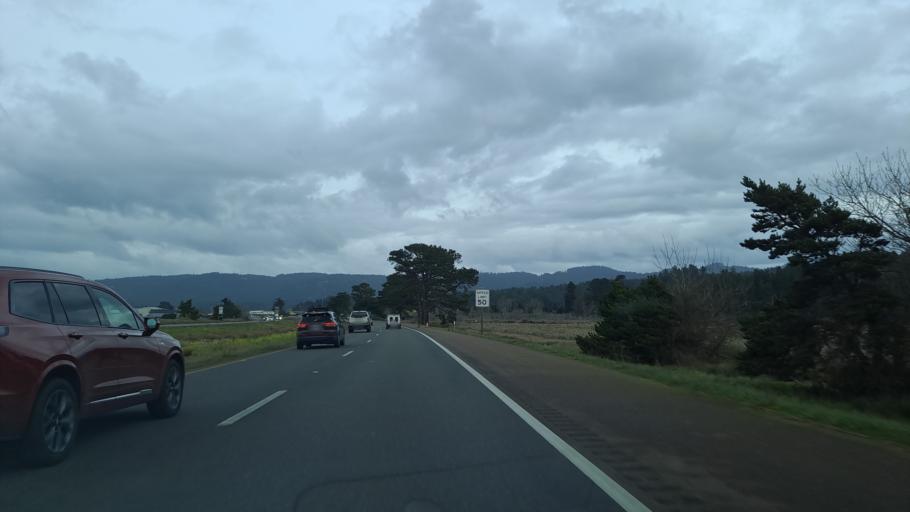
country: US
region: California
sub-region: Humboldt County
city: Bayside
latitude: 40.8220
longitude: -124.0900
